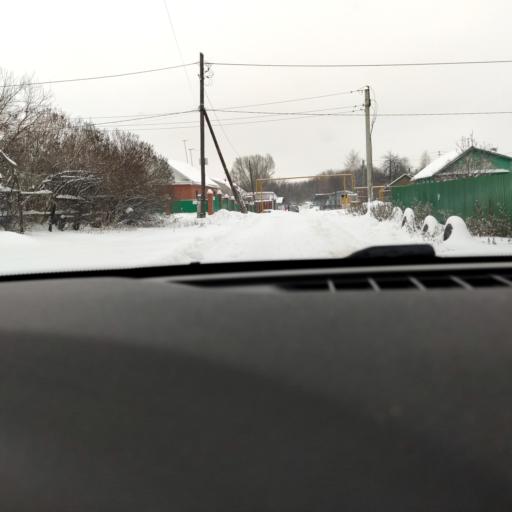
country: RU
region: Samara
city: Smyshlyayevka
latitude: 53.2423
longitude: 50.3460
